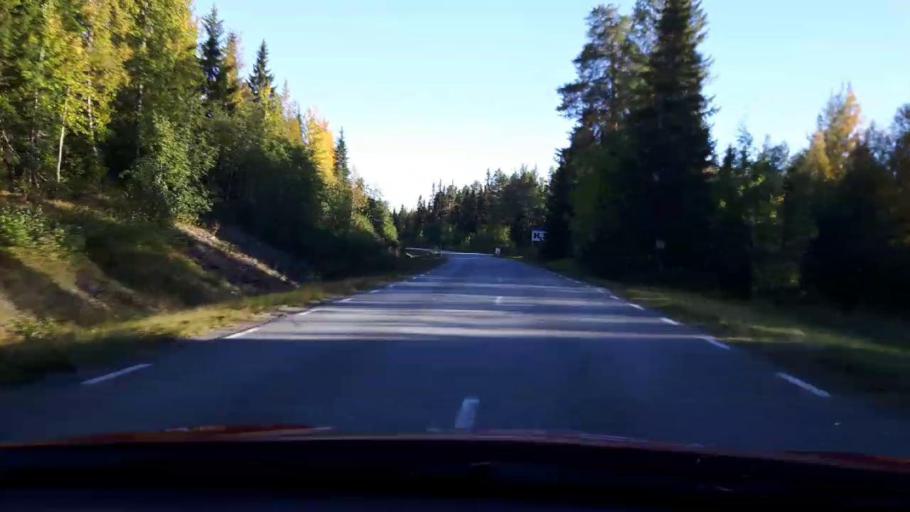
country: SE
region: Jaemtland
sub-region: OEstersunds Kommun
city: Lit
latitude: 63.7521
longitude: 14.7156
